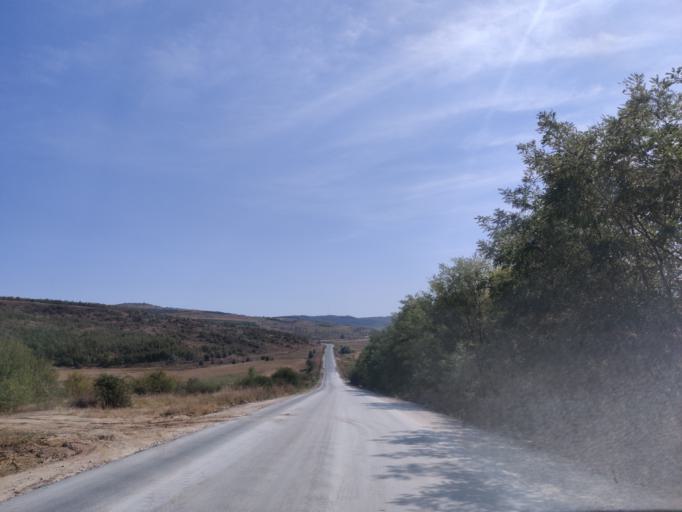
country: MD
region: Ungheni
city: Ungheni
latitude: 47.2537
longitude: 27.9970
